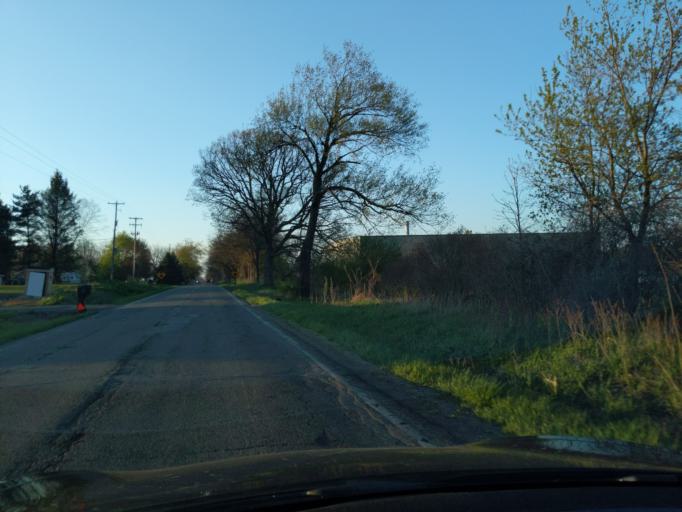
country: US
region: Michigan
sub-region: Jackson County
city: Jackson
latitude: 42.2734
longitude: -84.4831
